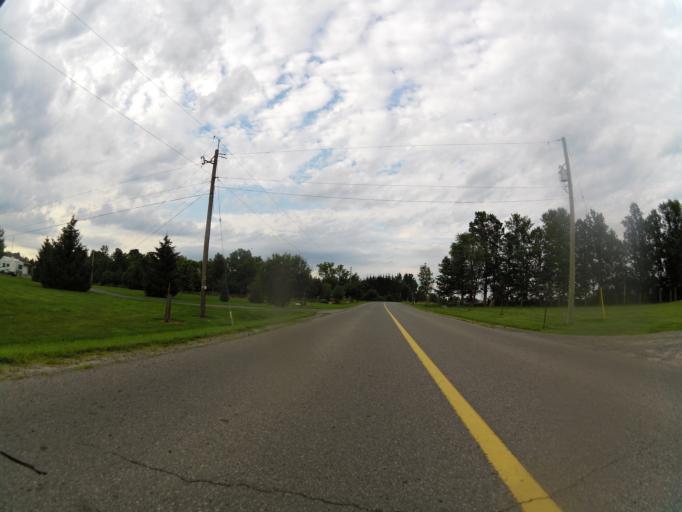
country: CA
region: Ontario
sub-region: Lanark County
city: Smiths Falls
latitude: 44.9942
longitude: -75.7627
